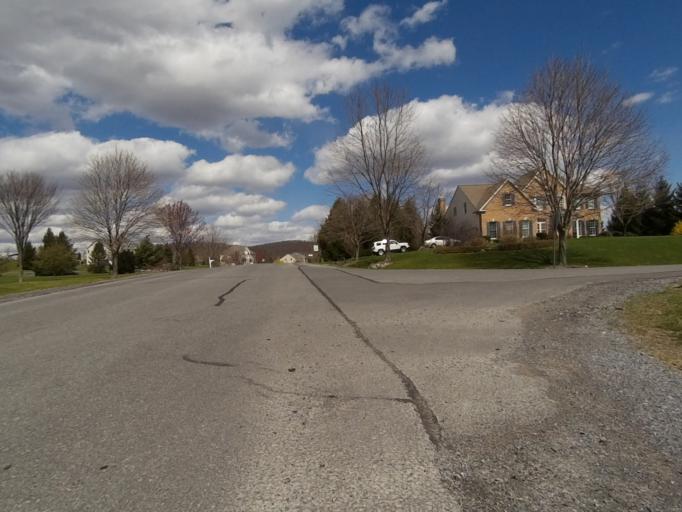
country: US
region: Pennsylvania
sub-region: Centre County
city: Park Forest Village
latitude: 40.8214
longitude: -77.9636
